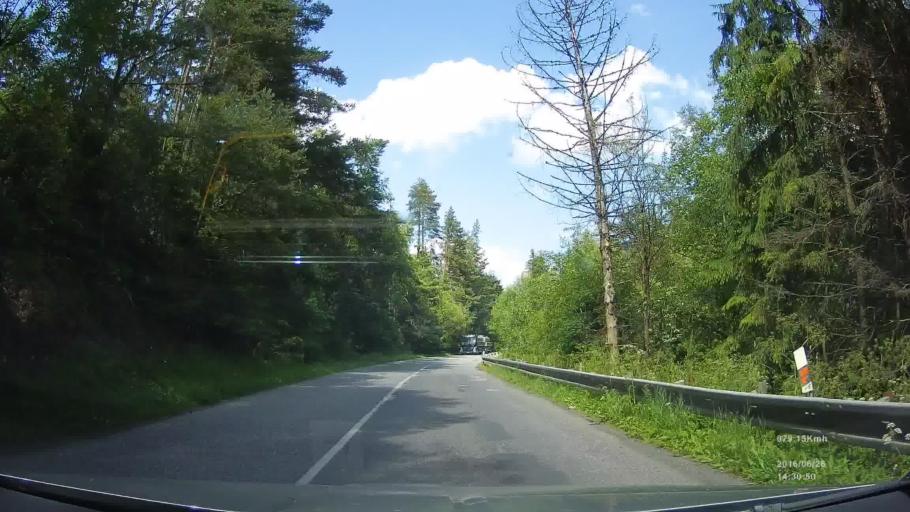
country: SK
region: Zilinsky
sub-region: Okres Zilina
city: Liptovsky Hradok
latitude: 48.9950
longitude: 19.7604
